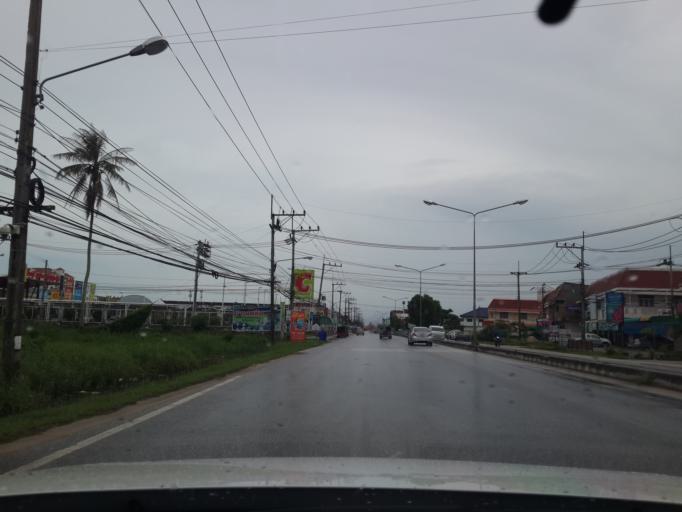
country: TH
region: Pattani
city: Pattani
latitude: 6.8603
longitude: 101.2306
